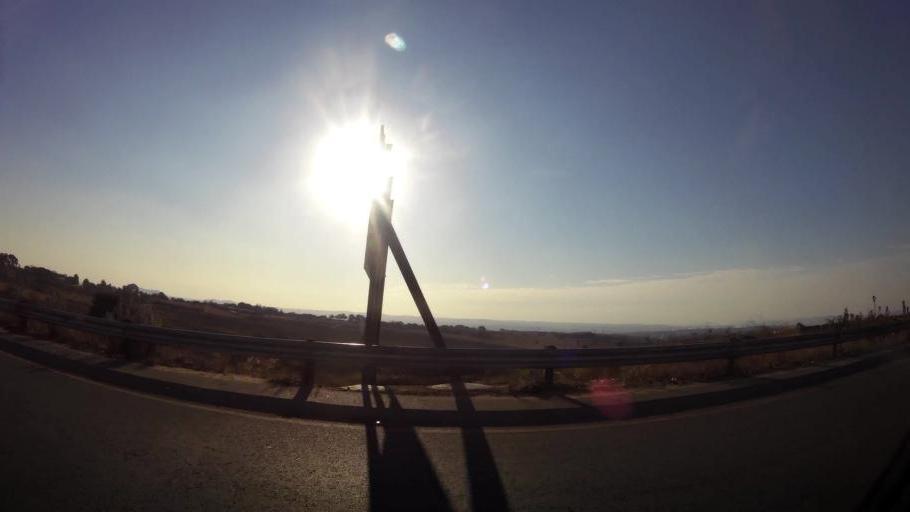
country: ZA
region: Gauteng
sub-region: West Rand District Municipality
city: Muldersdriseloop
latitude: -25.9972
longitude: 27.9245
